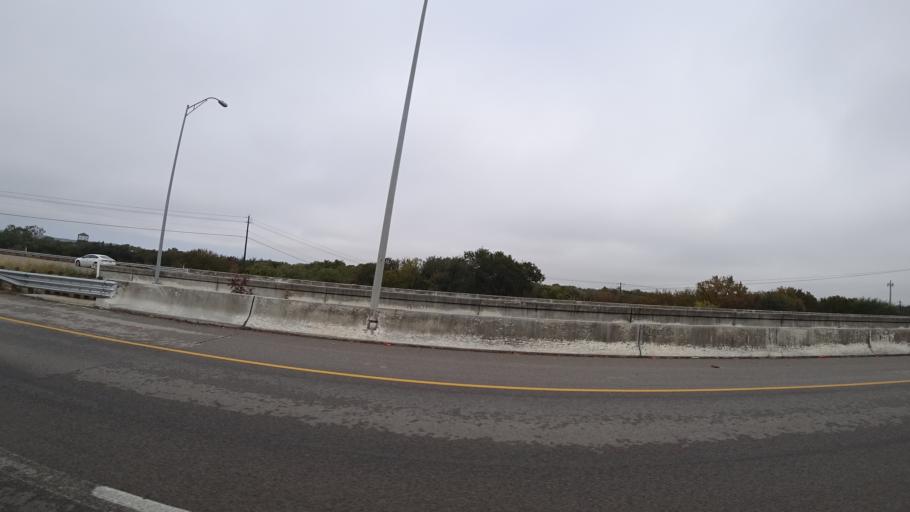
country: US
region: Texas
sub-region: Travis County
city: Shady Hollow
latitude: 30.2166
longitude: -97.8476
